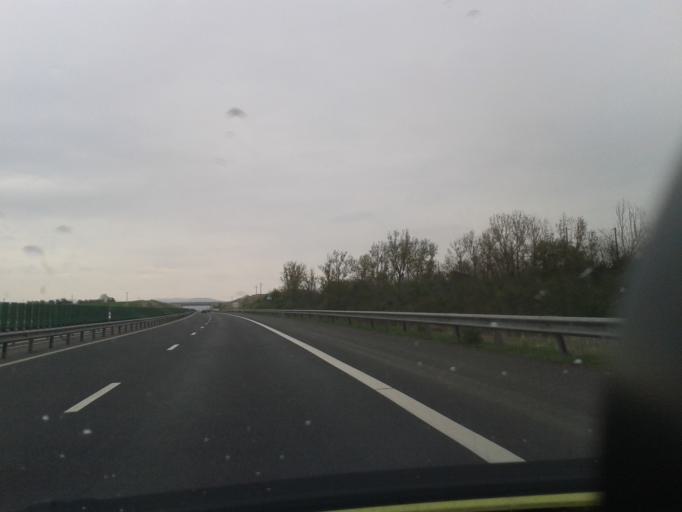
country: RO
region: Hunedoara
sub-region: Comuna Turdas
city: Turdas
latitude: 45.8414
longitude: 23.1238
